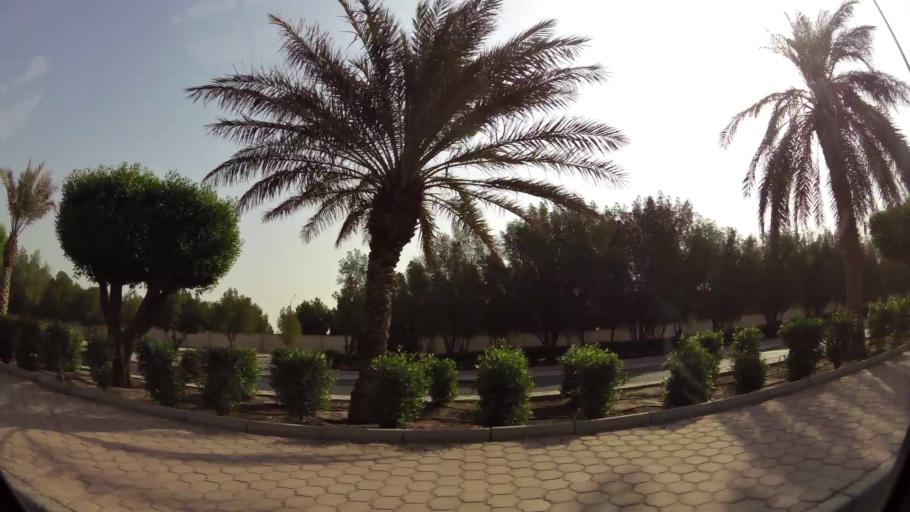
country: KW
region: Al Asimah
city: Ar Rabiyah
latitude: 29.3022
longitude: 47.8321
